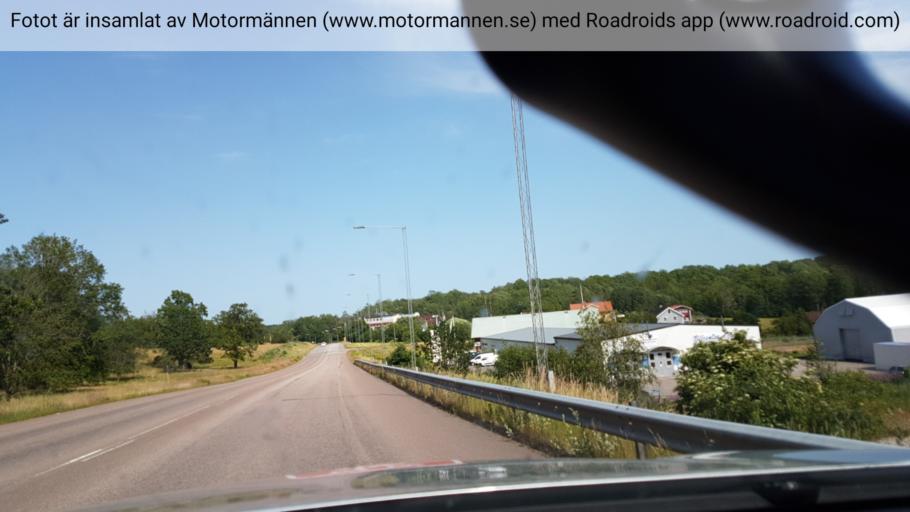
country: SE
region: Joenkoeping
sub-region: Tranas Kommun
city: Tranas
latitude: 58.0240
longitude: 14.9477
